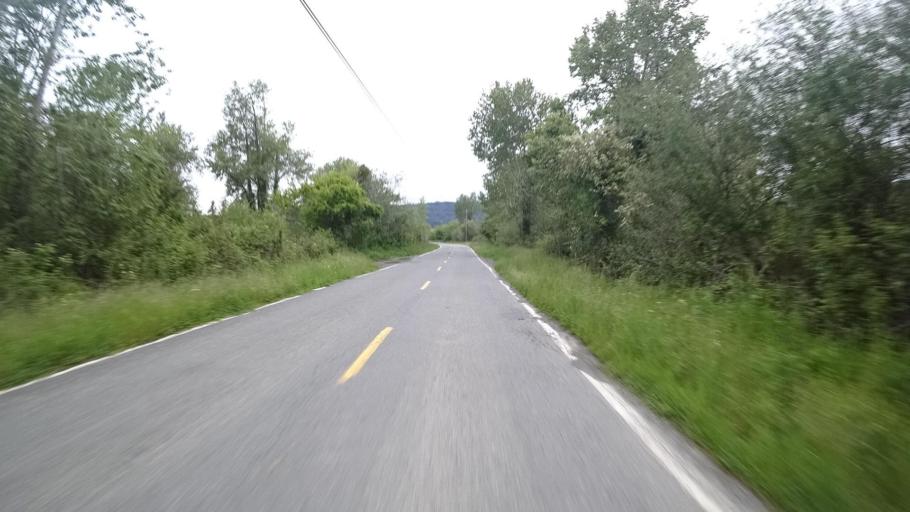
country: US
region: California
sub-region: Humboldt County
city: Blue Lake
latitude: 40.8690
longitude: -123.9951
